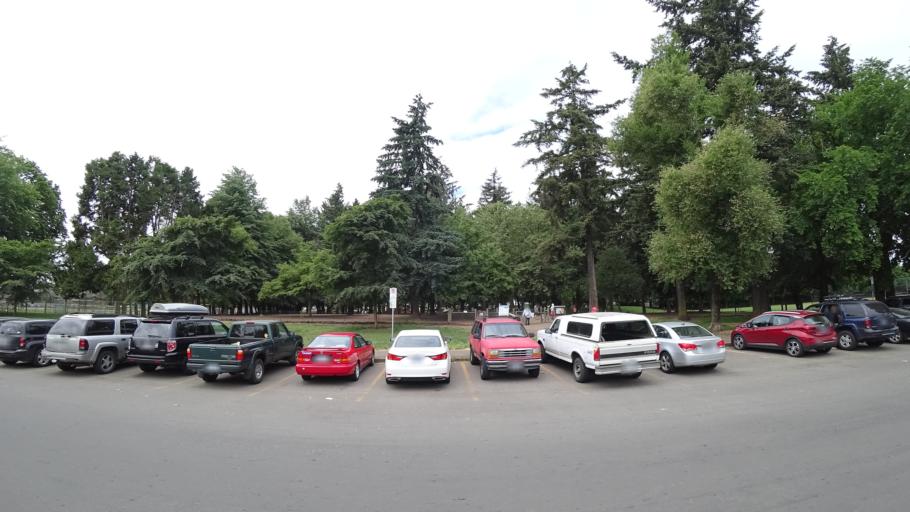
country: US
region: Oregon
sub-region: Multnomah County
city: Lents
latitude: 45.5317
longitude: -122.6051
